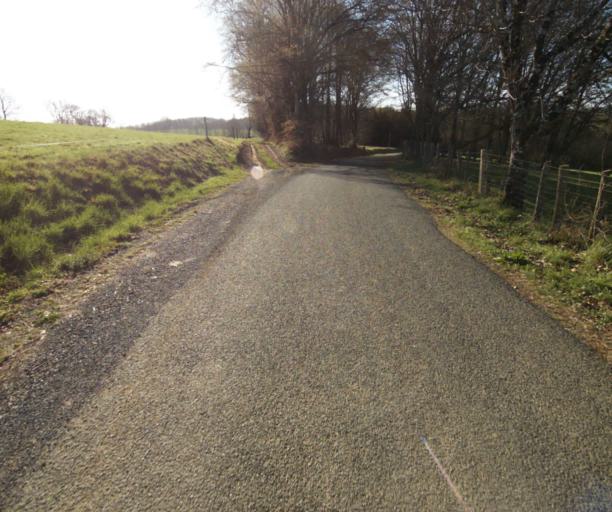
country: FR
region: Limousin
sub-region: Departement de la Correze
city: Seilhac
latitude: 45.3704
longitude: 1.7519
